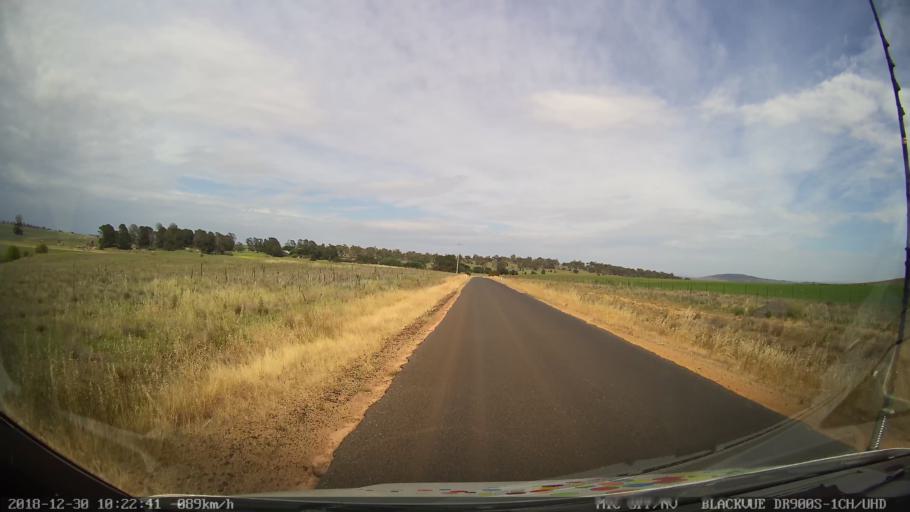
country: AU
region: New South Wales
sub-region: Snowy River
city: Berridale
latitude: -36.5426
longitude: 148.9914
